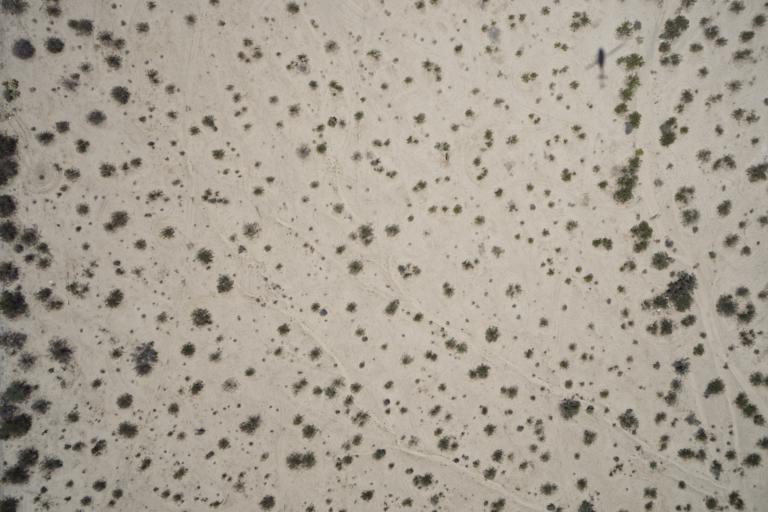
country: US
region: California
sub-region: San Bernardino County
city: Twentynine Palms
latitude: 34.1366
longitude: -116.0421
